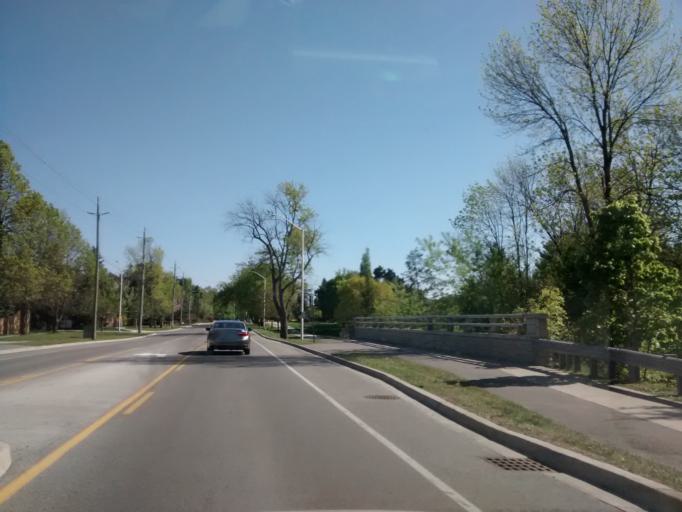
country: CA
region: Ontario
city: Oakville
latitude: 43.3820
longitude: -79.7174
